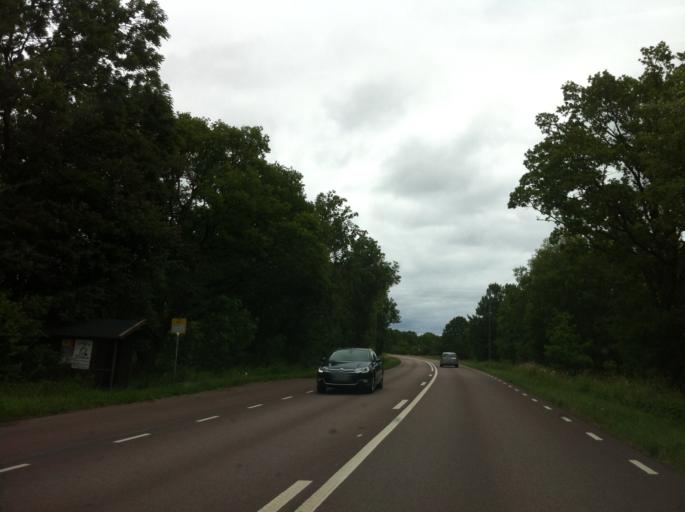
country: SE
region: Kalmar
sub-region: Borgholms Kommun
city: Borgholm
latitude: 57.1966
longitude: 17.0416
